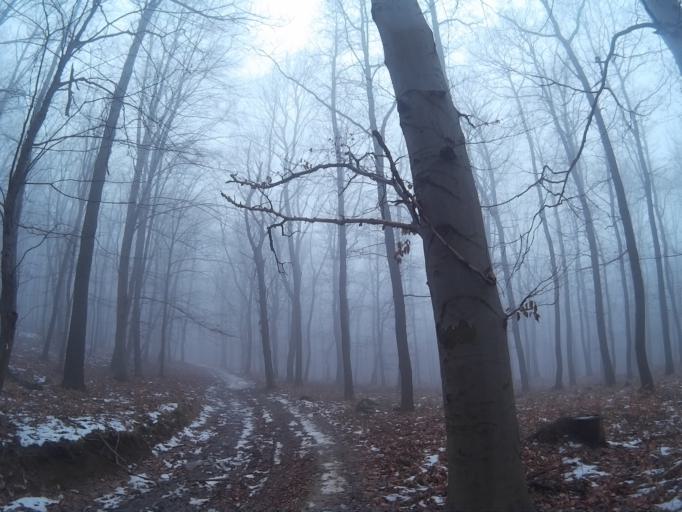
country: HU
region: Komarom-Esztergom
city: Tardos
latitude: 47.6843
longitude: 18.4753
